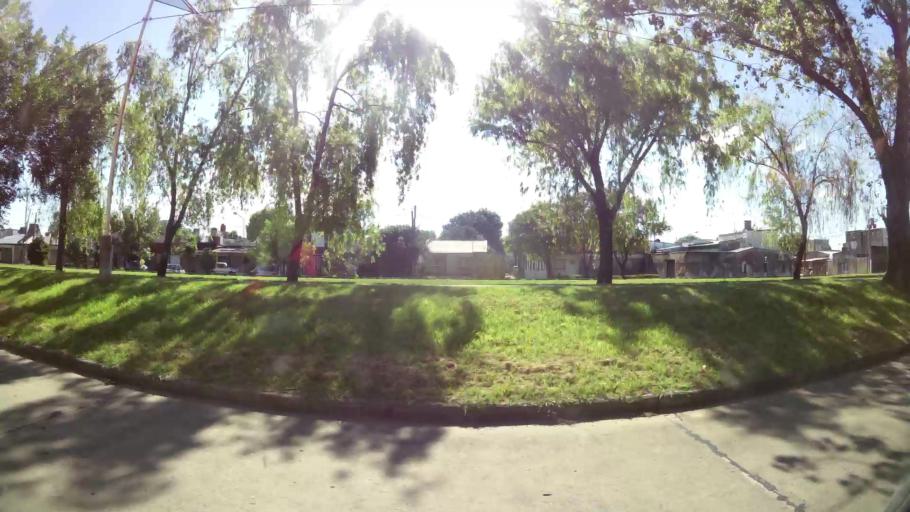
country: AR
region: Santa Fe
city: Santa Fe de la Vera Cruz
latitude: -31.6150
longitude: -60.6787
